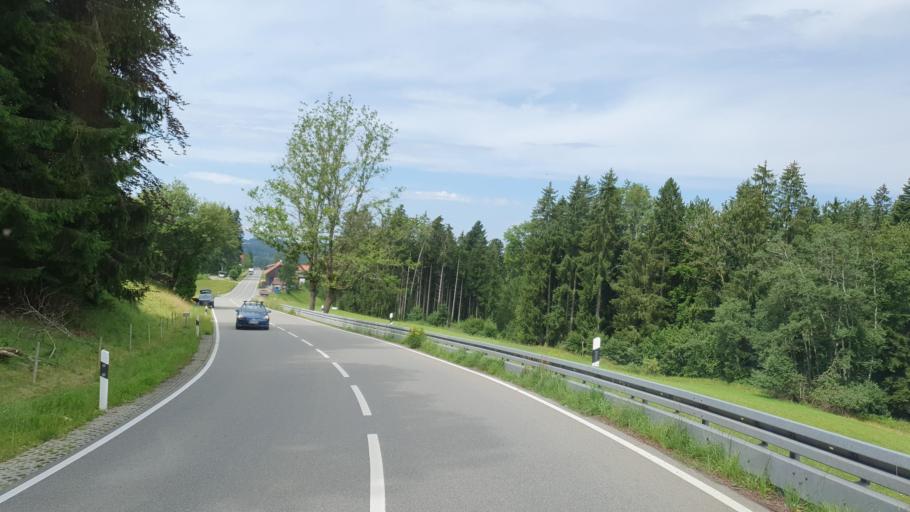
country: AT
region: Vorarlberg
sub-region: Politischer Bezirk Bregenz
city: Hohenweiler
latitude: 47.5980
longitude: 9.8053
